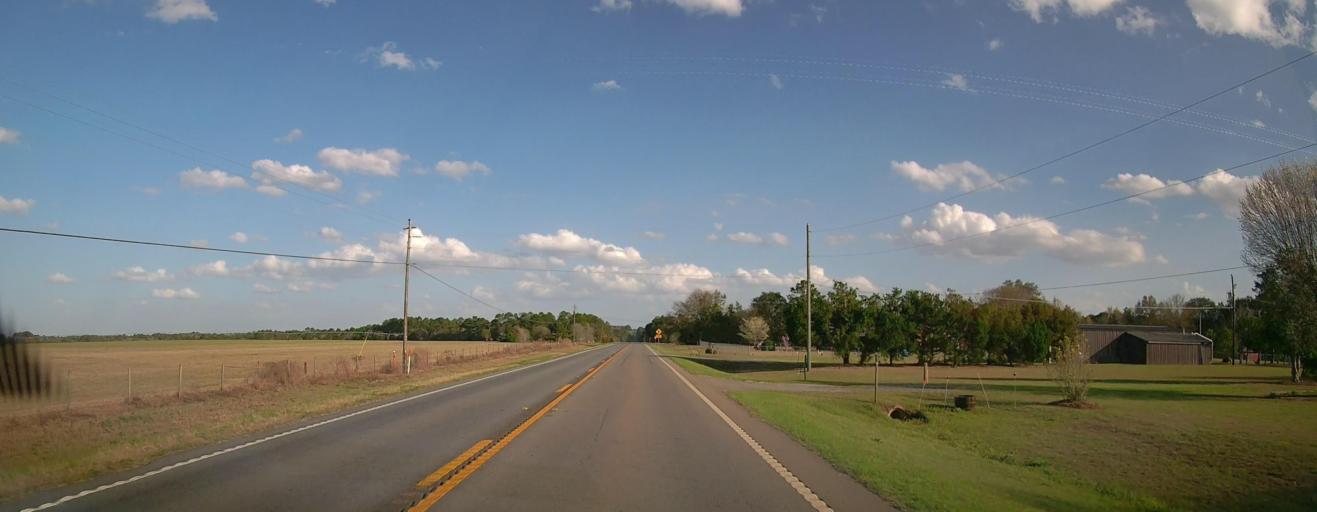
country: US
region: Georgia
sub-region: Tattnall County
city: Reidsville
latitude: 32.0977
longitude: -82.1586
